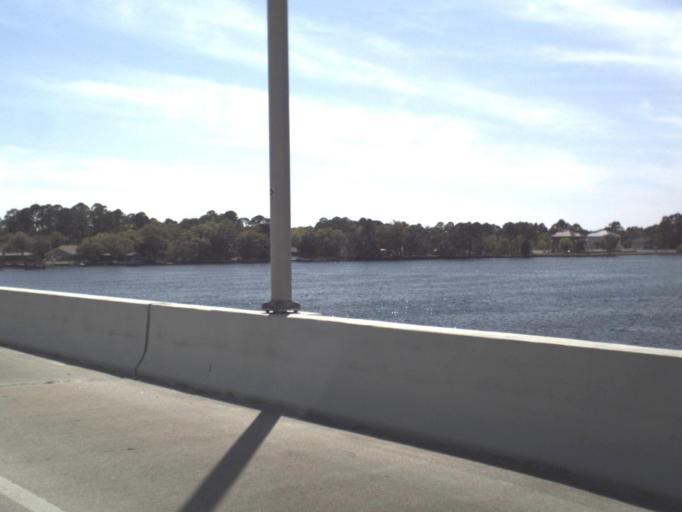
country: US
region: Florida
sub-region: Bay County
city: Lynn Haven
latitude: 30.2588
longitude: -85.6469
